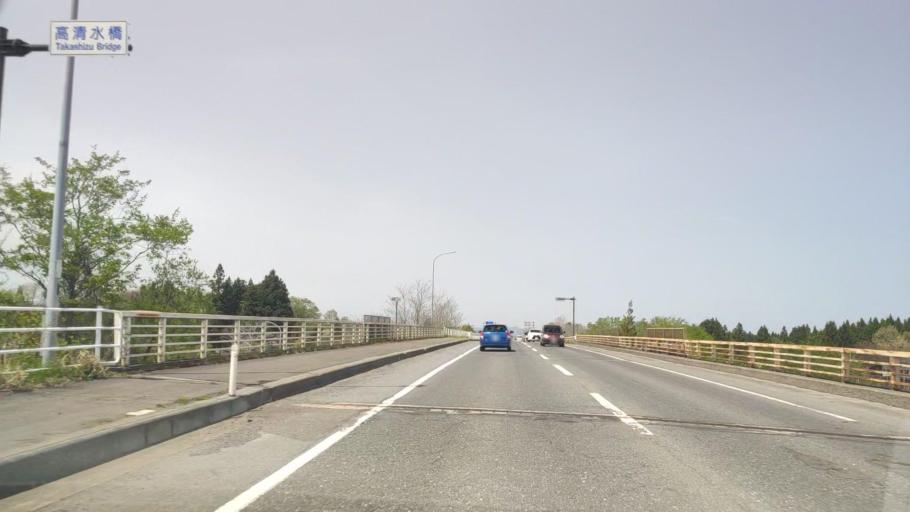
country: JP
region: Aomori
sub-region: Misawa Shi
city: Inuotose
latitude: 40.6309
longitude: 141.2482
